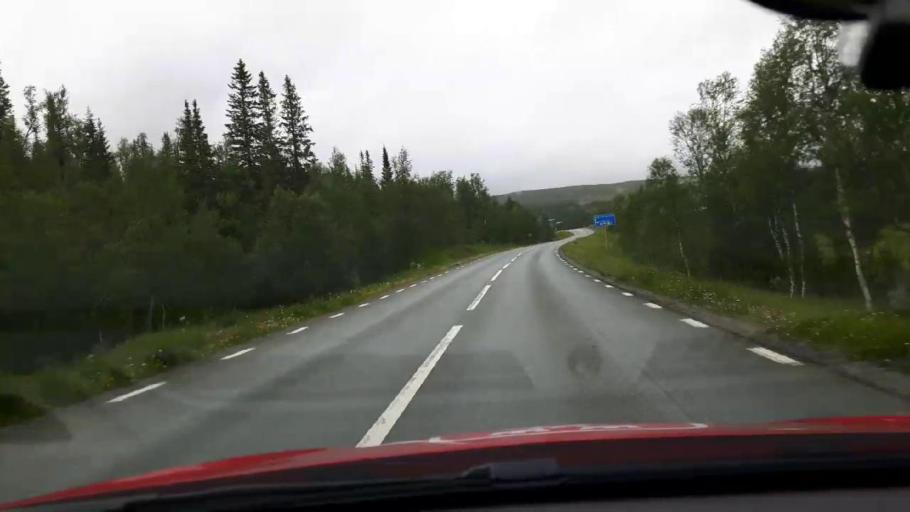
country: NO
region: Nord-Trondelag
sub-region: Meraker
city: Meraker
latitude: 63.3060
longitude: 12.1089
